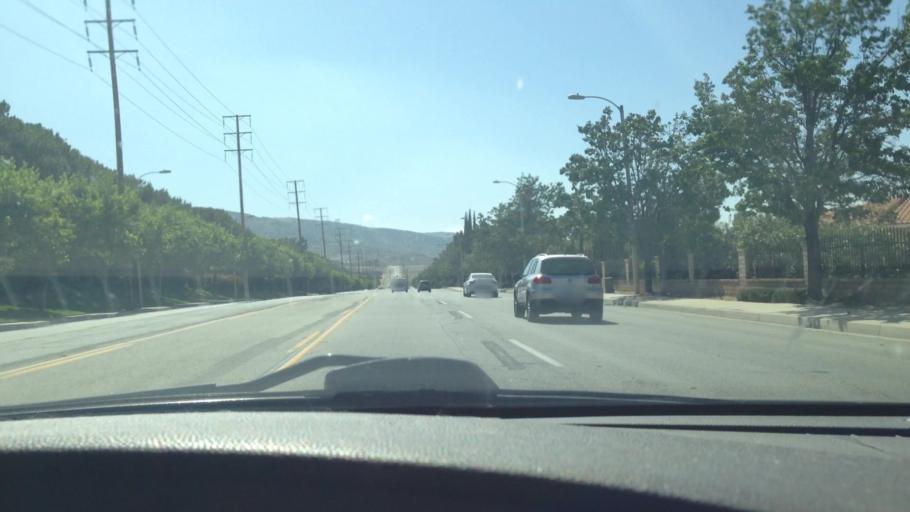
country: US
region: California
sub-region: Los Angeles County
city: Quartz Hill
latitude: 34.6309
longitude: -118.2287
